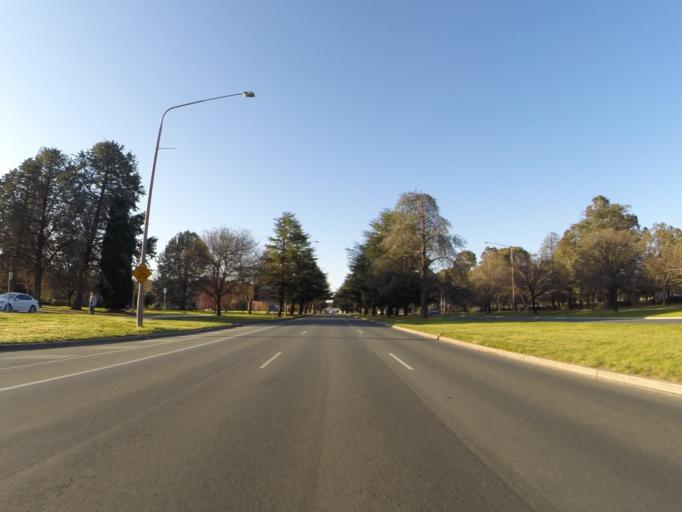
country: AU
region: Australian Capital Territory
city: Forrest
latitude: -35.2999
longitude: 149.1257
